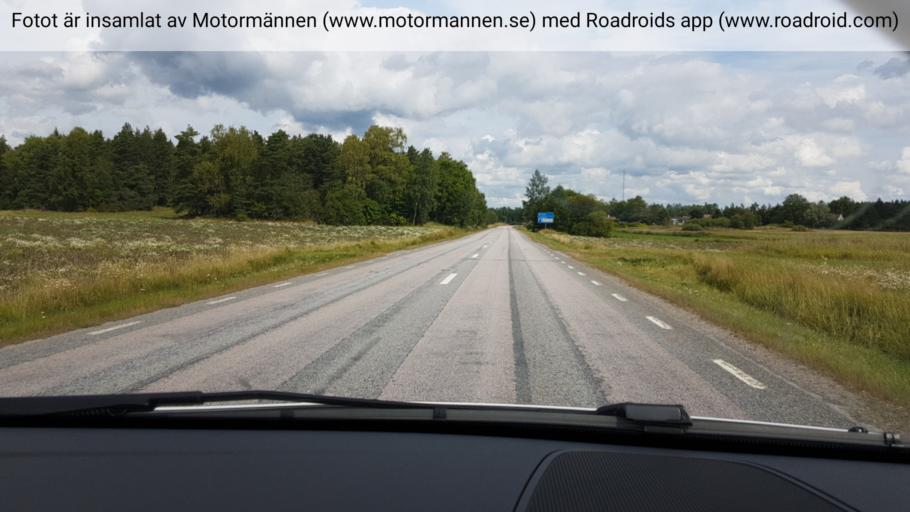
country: SE
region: Stockholm
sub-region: Norrtalje Kommun
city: Nykvarn
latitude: 59.9234
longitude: 18.1073
